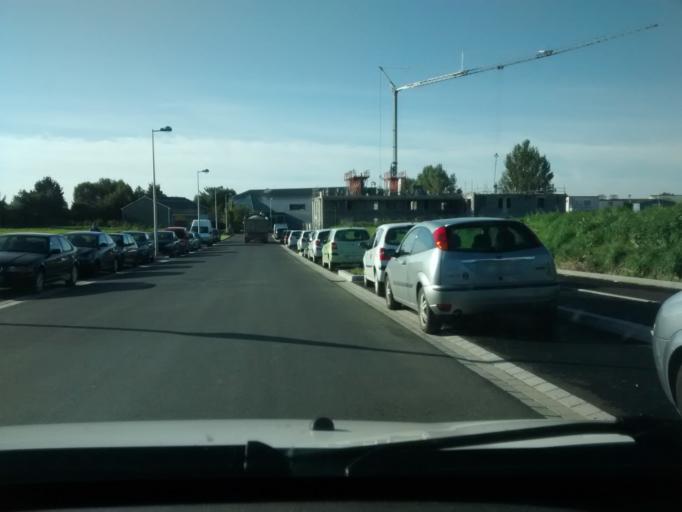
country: FR
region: Brittany
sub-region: Departement d'Ille-et-Vilaine
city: Saint-Malo
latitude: 48.6549
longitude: -1.9695
